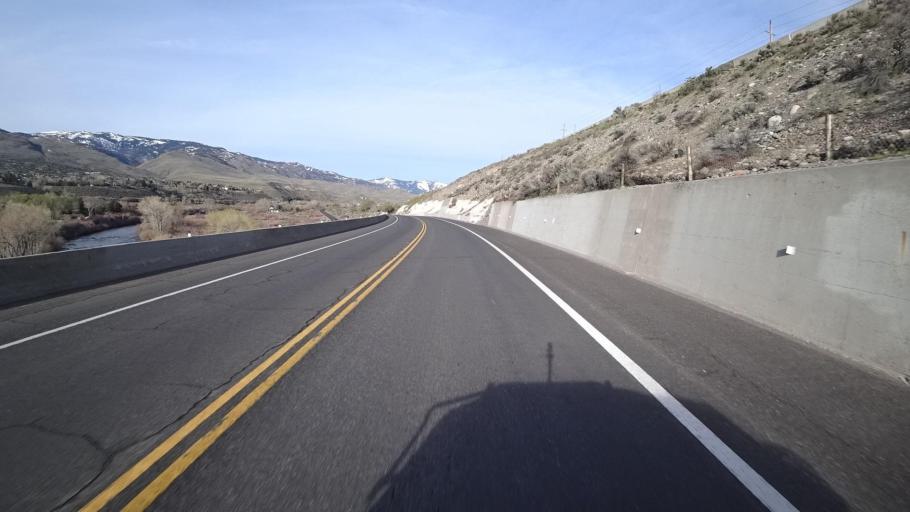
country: US
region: Nevada
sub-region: Washoe County
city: Mogul
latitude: 39.5110
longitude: -119.8753
